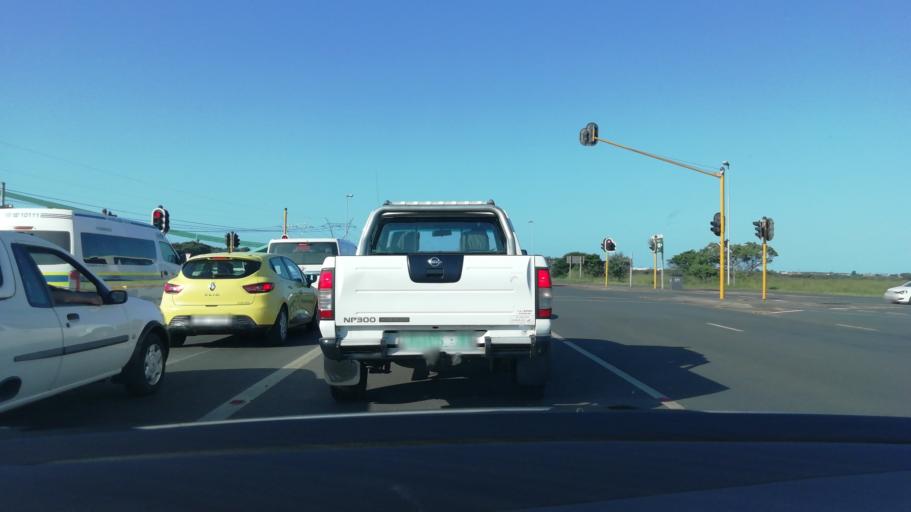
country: ZA
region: KwaZulu-Natal
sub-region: uThungulu District Municipality
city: Richards Bay
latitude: -28.7687
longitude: 32.0354
